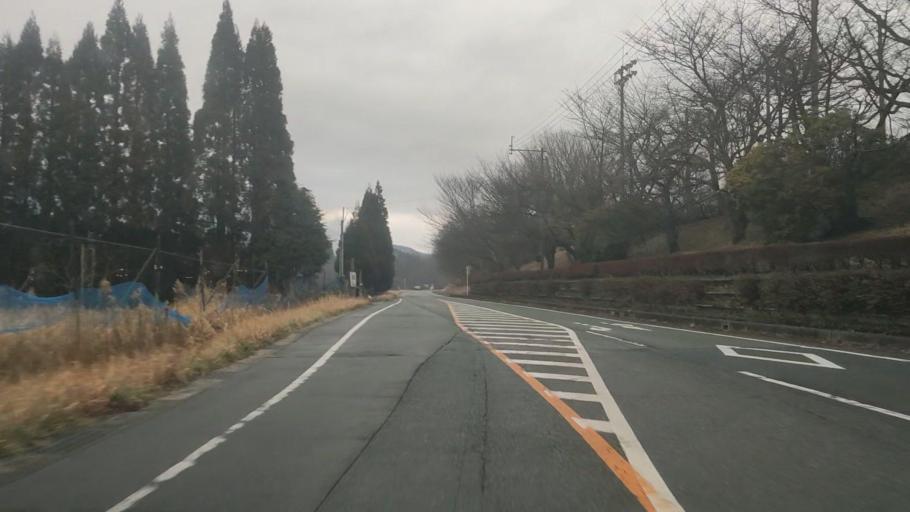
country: JP
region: Kumamoto
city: Aso
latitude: 32.8472
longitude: 131.1485
